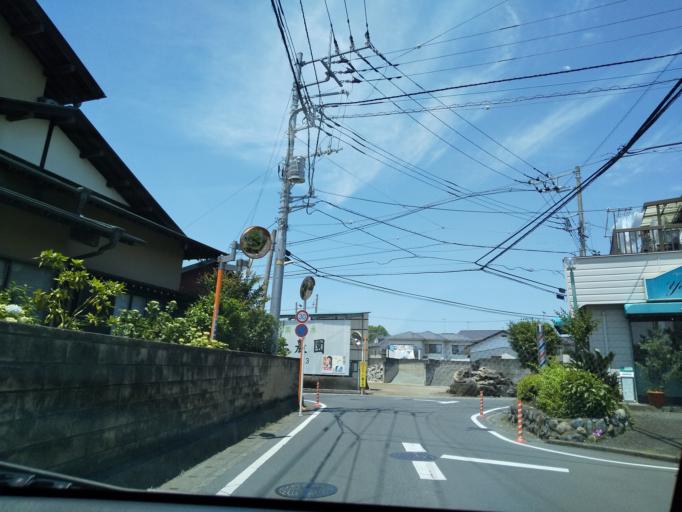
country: JP
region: Kanagawa
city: Zama
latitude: 35.5263
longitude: 139.3807
